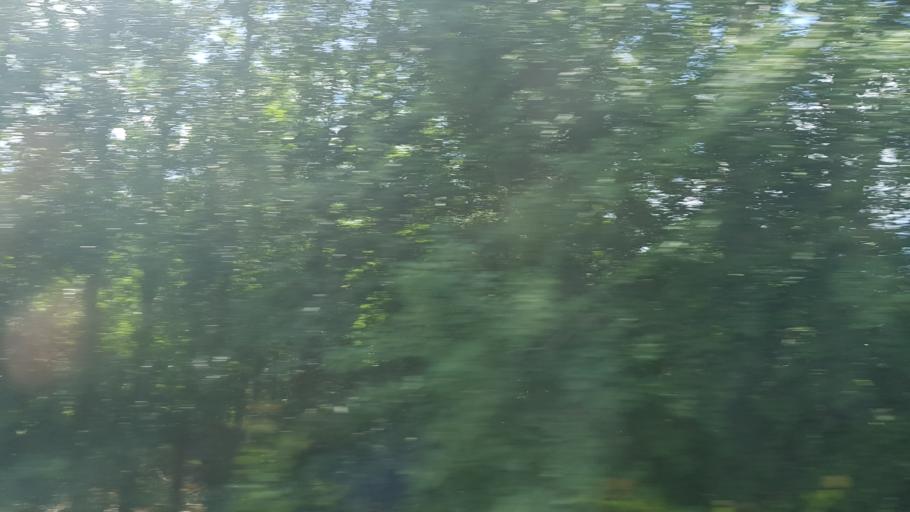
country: SE
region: Vaestra Goetaland
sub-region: Kungalvs Kommun
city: Kode
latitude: 57.9400
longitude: 11.8556
